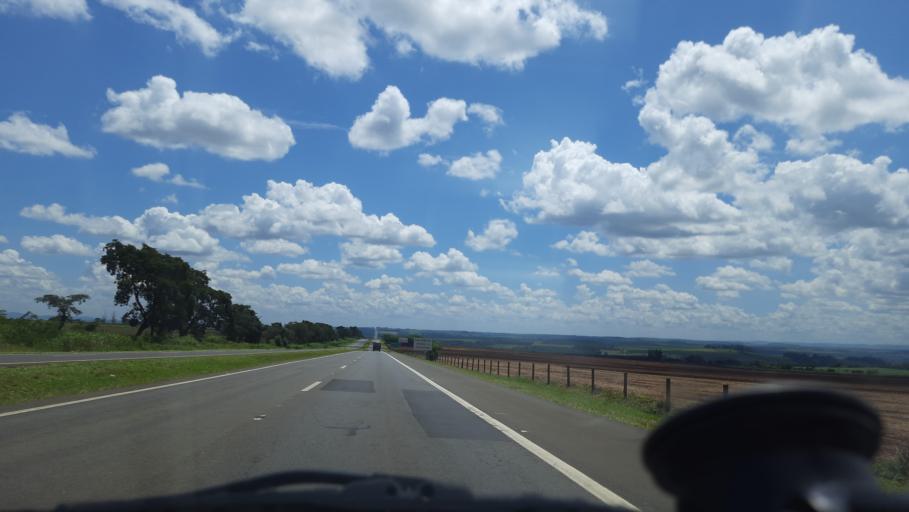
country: BR
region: Sao Paulo
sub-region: Aguai
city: Aguai
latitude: -22.0338
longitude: -47.0323
